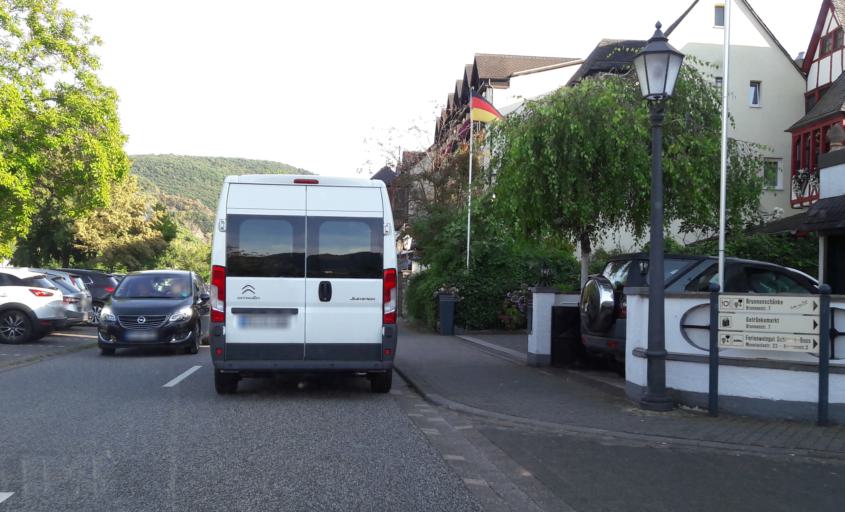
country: DE
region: Rheinland-Pfalz
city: Bruttig-Fankel
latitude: 50.1177
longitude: 7.2322
